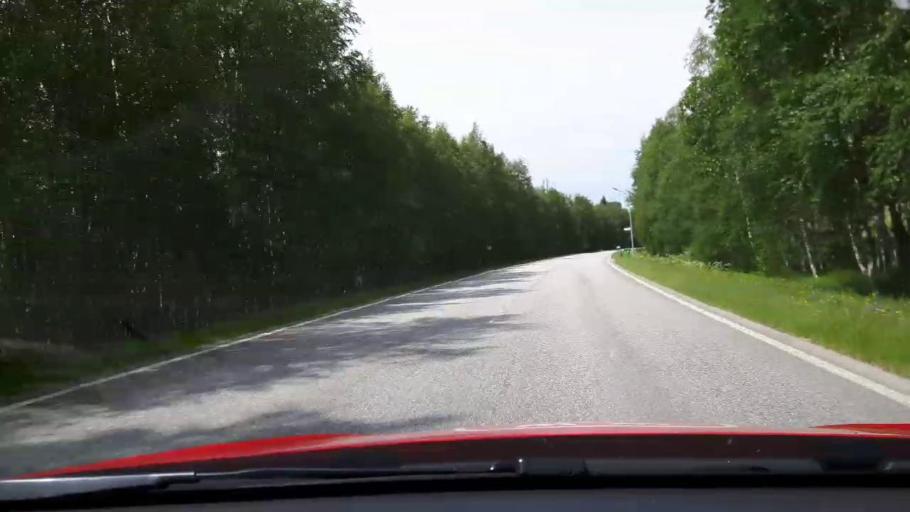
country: SE
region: Jaemtland
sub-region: Harjedalens Kommun
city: Sveg
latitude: 62.1299
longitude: 14.0602
